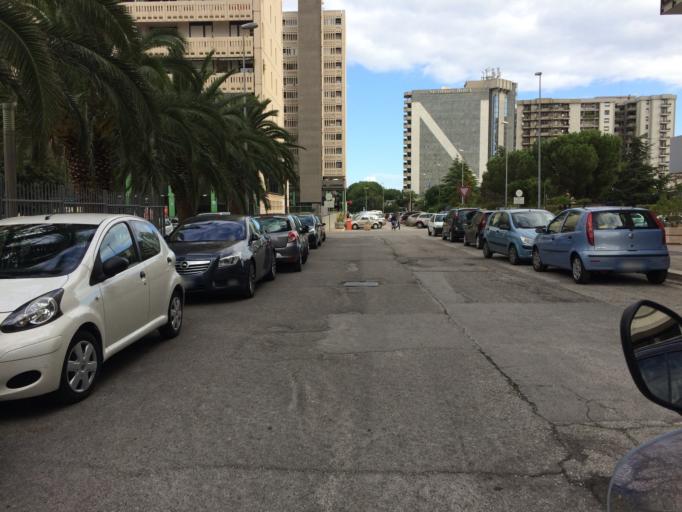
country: IT
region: Apulia
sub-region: Provincia di Bari
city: Bari
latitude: 41.0971
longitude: 16.8535
